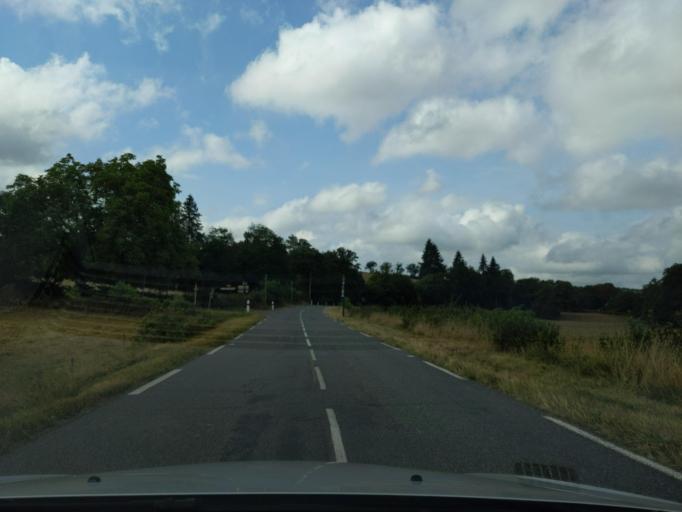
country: FR
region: Bourgogne
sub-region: Departement de la Nievre
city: Luzy
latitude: 46.7282
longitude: 3.9166
